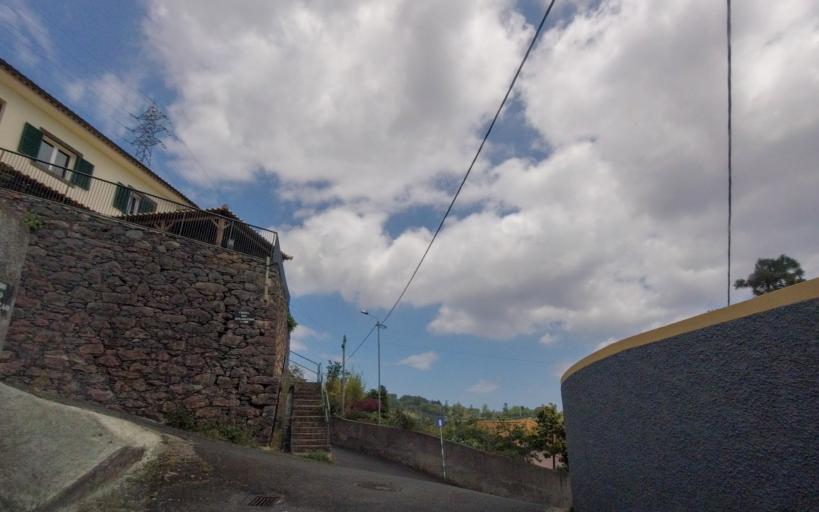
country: PT
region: Madeira
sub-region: Funchal
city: Nossa Senhora do Monte
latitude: 32.6629
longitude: -16.8797
